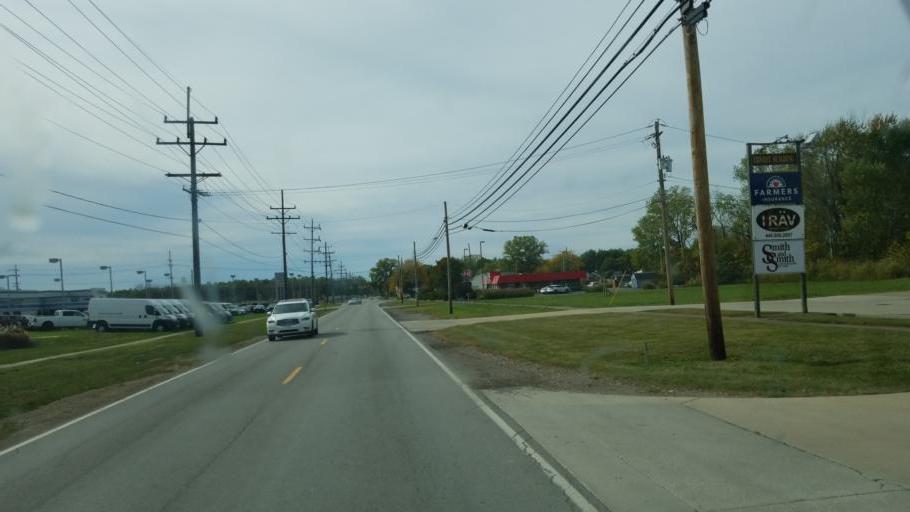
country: US
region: Ohio
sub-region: Lorain County
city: Avon Lake
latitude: 41.4935
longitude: -82.0587
